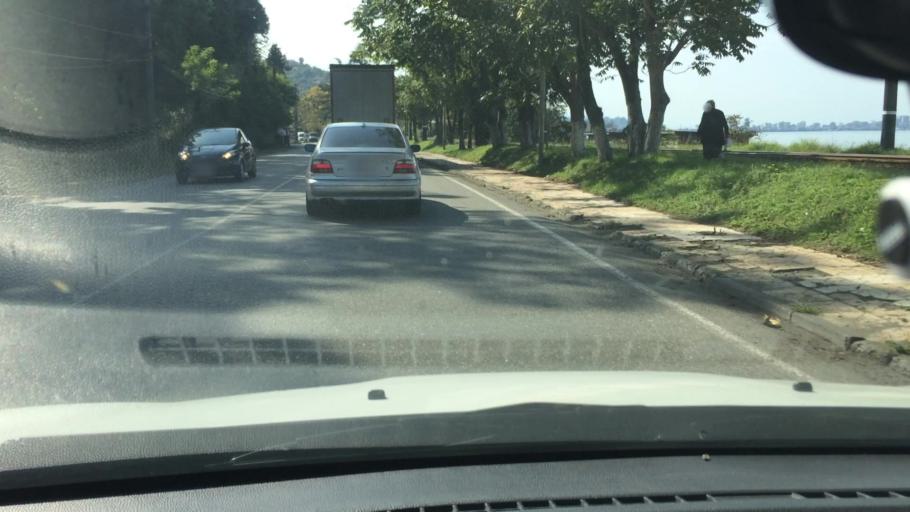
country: GE
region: Ajaria
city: Makhinjauri
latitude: 41.6818
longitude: 41.6988
